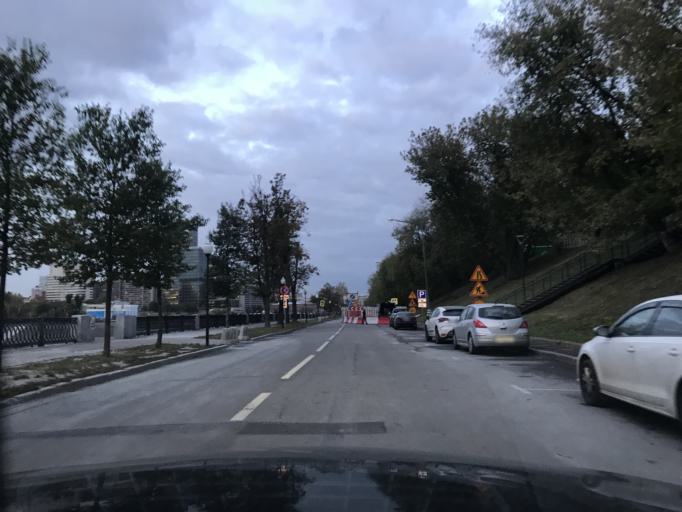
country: RU
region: Moskovskaya
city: Presnenskiy
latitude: 55.7481
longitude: 37.5495
